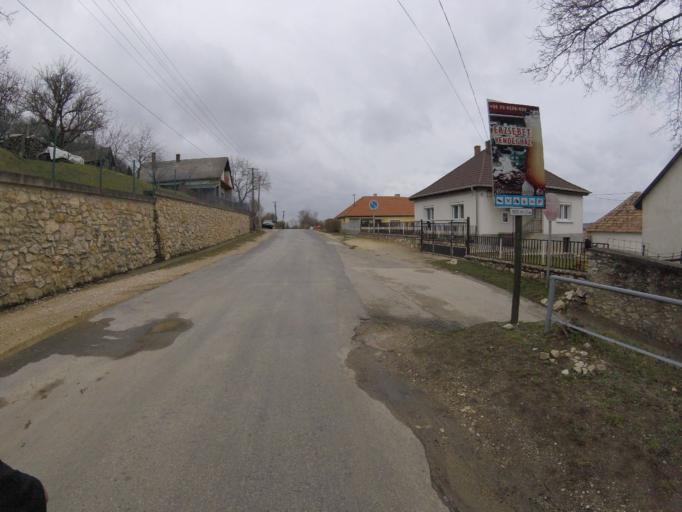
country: HU
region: Veszprem
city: Zirc
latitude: 47.3511
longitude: 17.8851
